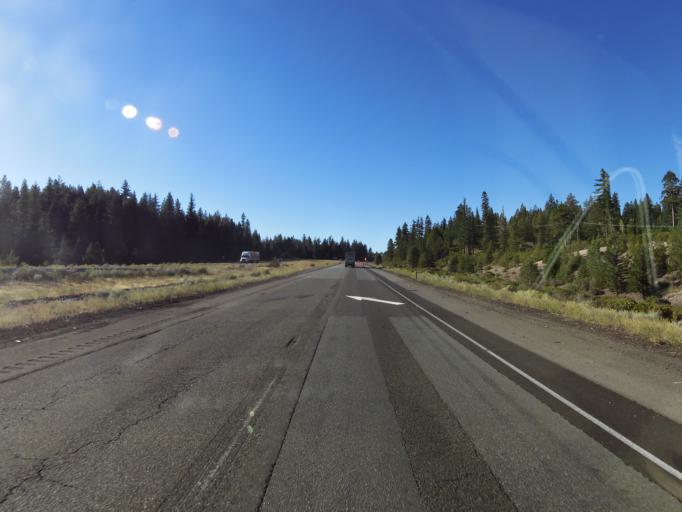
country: US
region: California
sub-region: Siskiyou County
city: Weed
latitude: 41.3685
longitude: -122.3704
